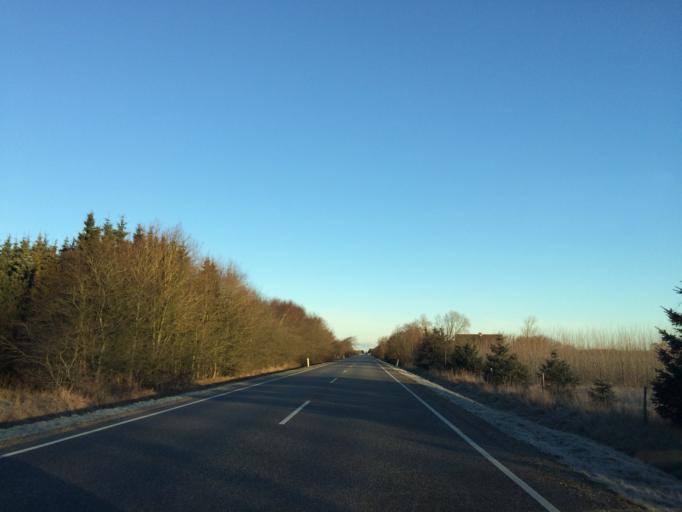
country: DK
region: Central Jutland
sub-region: Holstebro Kommune
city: Ulfborg
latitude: 56.3822
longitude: 8.3267
